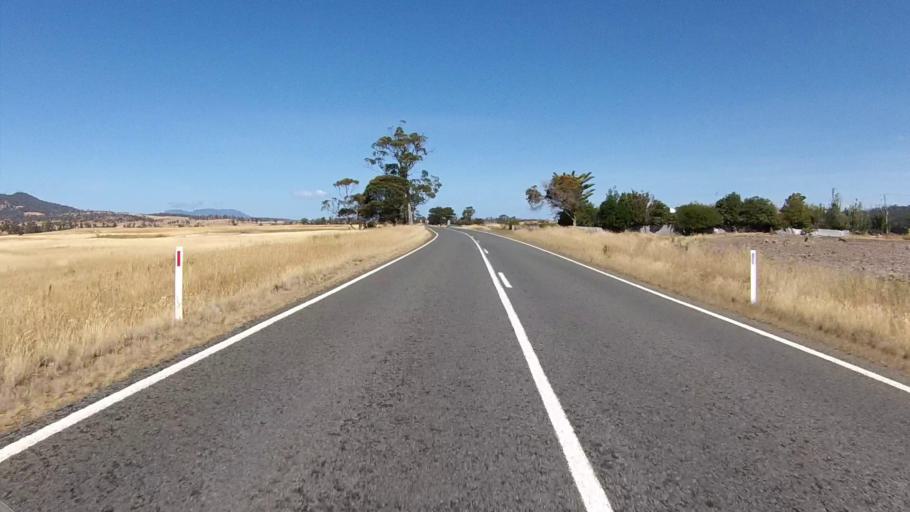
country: AU
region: Tasmania
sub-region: Sorell
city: Sorell
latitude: -42.4448
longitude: 147.9284
